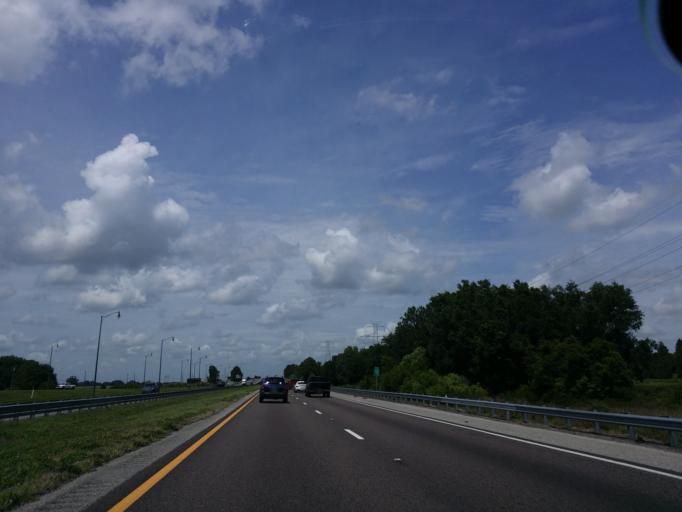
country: US
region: Florida
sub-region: Lake County
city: Hawthorne
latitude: 28.7577
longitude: -81.9411
